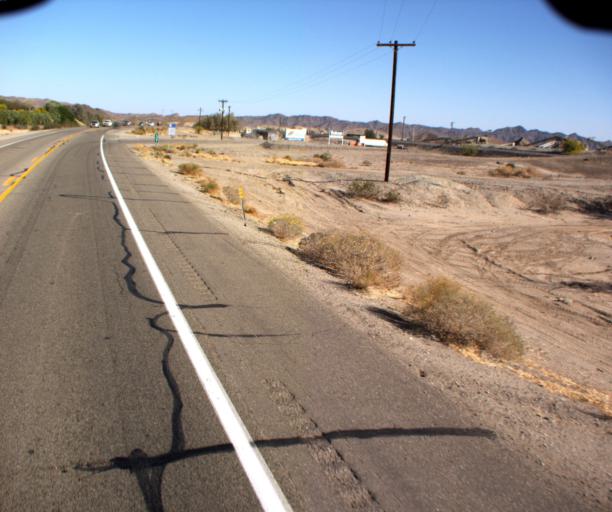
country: US
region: Arizona
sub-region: Yuma County
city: Fortuna Foothills
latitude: 32.7368
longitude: -114.4249
